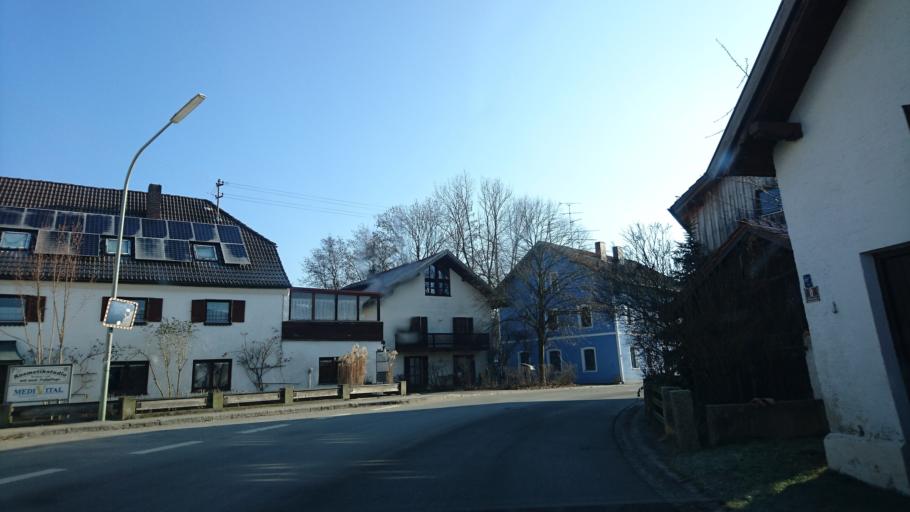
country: DE
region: Bavaria
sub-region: Lower Bavaria
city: Bad Griesbach
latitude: 48.4201
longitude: 13.2129
